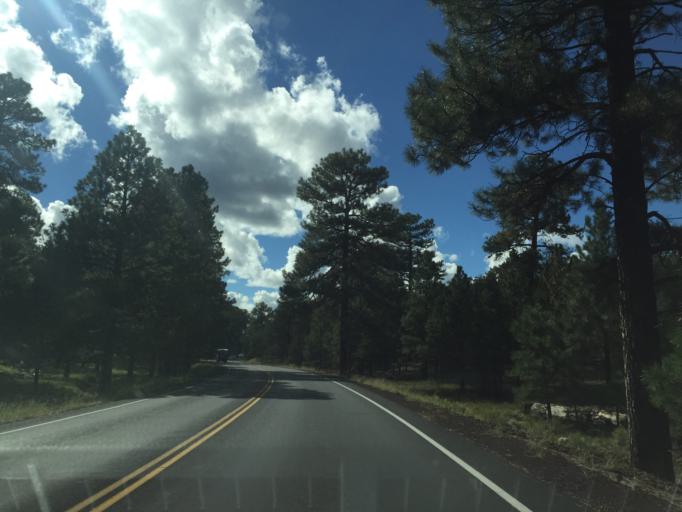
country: US
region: Arizona
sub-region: Coconino County
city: Grand Canyon
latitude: 36.0564
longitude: -112.1313
